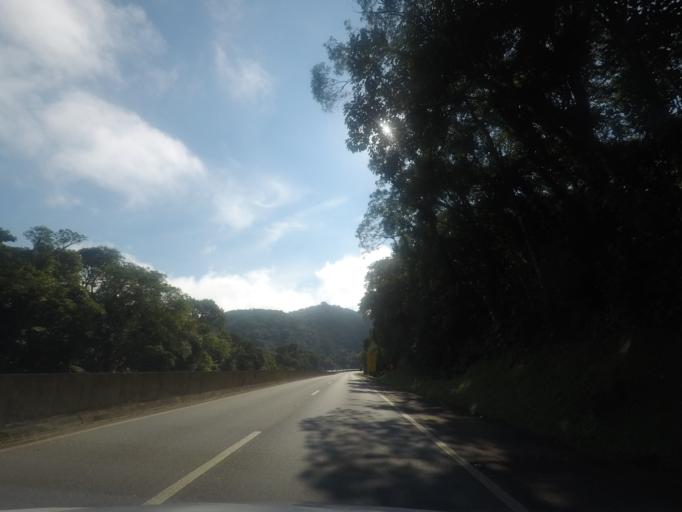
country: BR
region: Parana
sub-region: Piraquara
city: Piraquara
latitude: -25.5934
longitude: -48.8961
